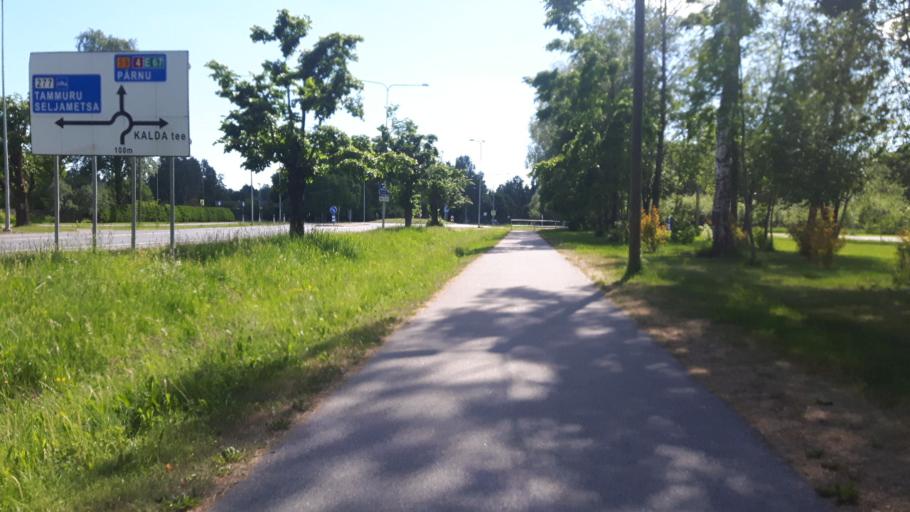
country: EE
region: Paernumaa
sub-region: Paikuse vald
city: Paikuse
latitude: 58.3766
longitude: 24.6239
